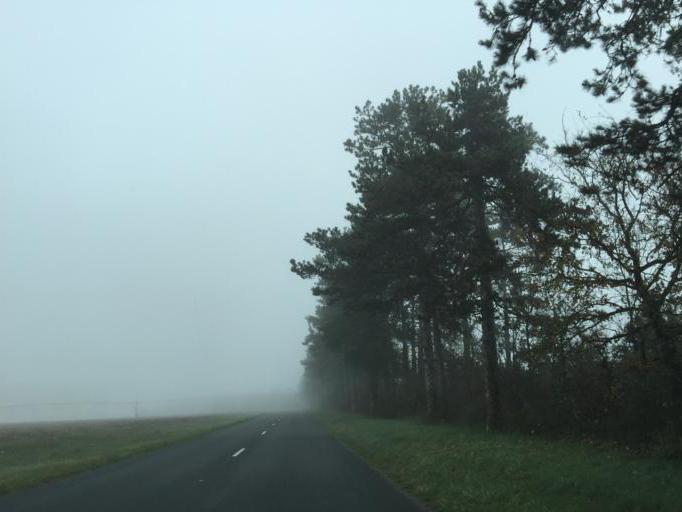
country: FR
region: Rhone-Alpes
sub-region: Departement de l'Ain
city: Chazey-sur-Ain
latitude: 45.8648
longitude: 5.2877
